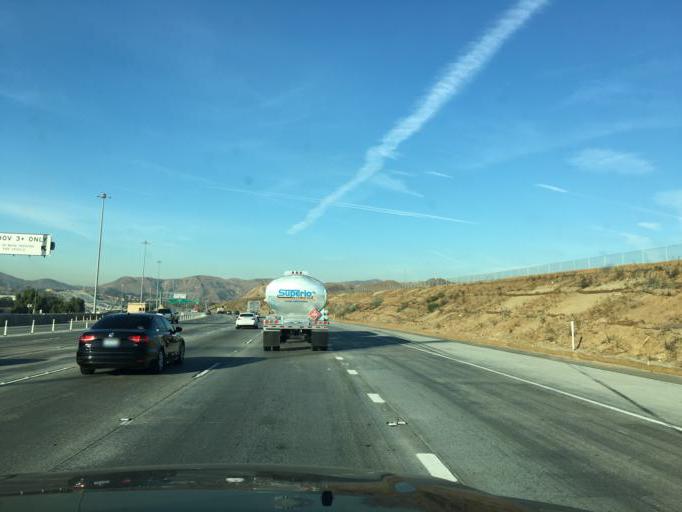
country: US
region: California
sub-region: Riverside County
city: Corona
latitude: 33.8851
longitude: -117.6320
